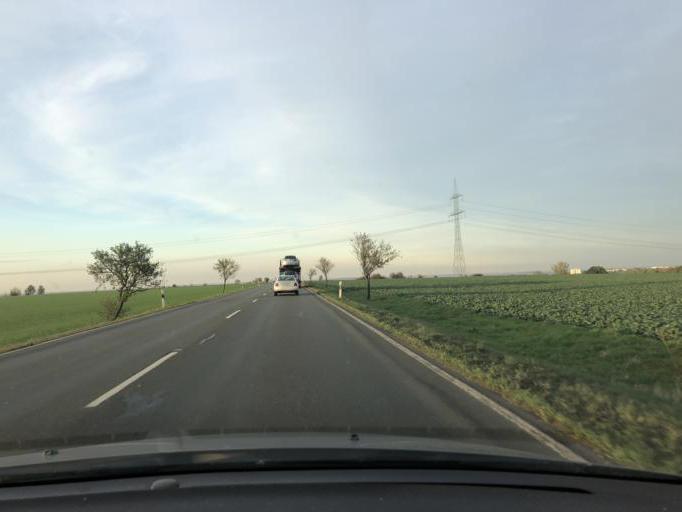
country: DE
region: Saxony-Anhalt
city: Zeitz
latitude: 51.0141
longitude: 12.1233
